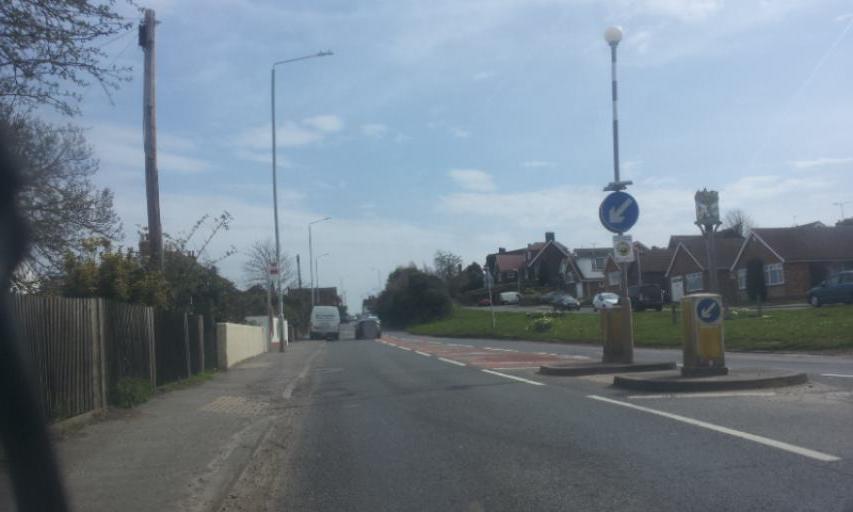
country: GB
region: England
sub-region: Kent
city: Newington
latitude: 51.3527
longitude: 0.6635
